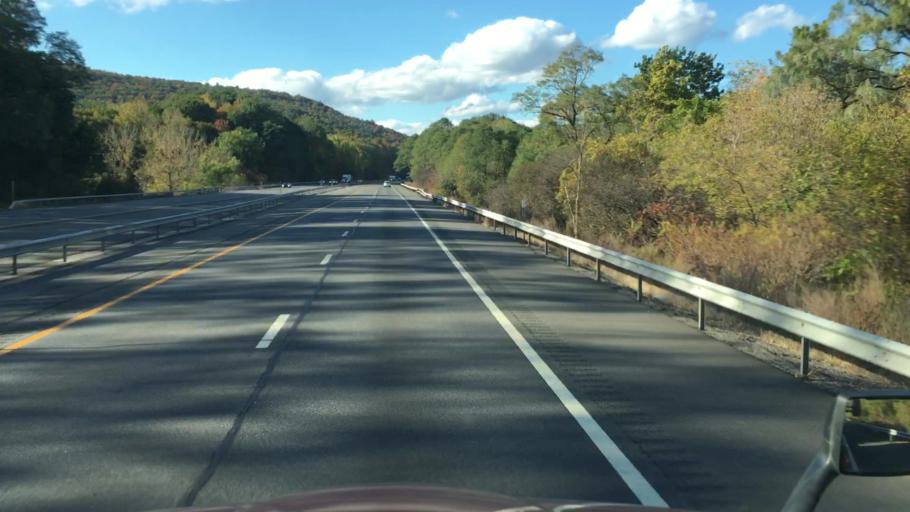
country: US
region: New York
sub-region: Schenectady County
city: Scotia
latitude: 42.8493
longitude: -74.0253
